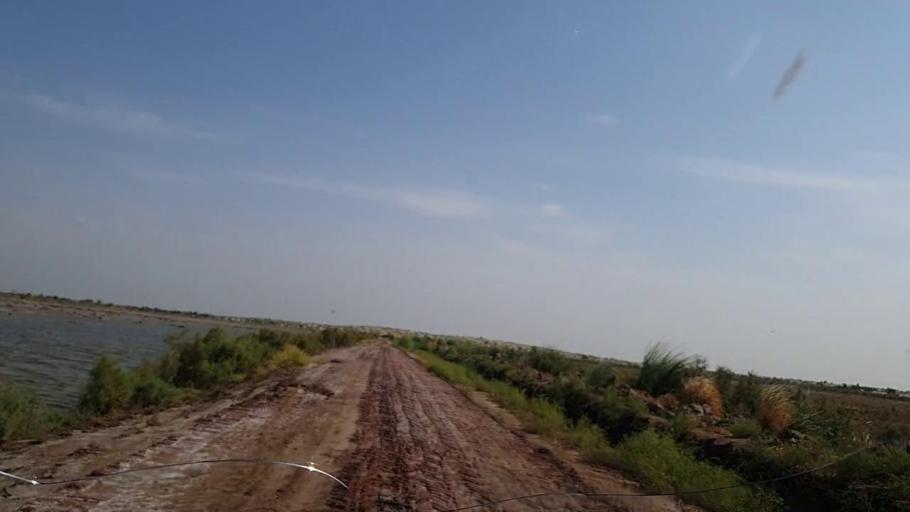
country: PK
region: Sindh
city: Khanpur
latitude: 27.6812
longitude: 69.3682
